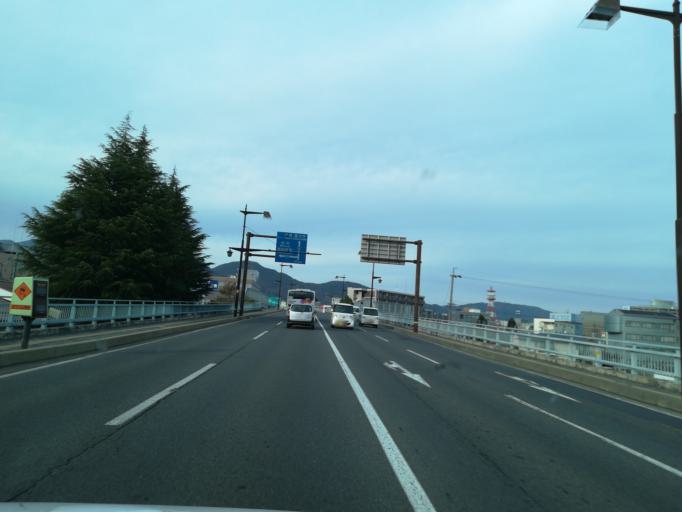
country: JP
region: Nagano
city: Nagano-shi
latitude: 36.6380
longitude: 138.1818
